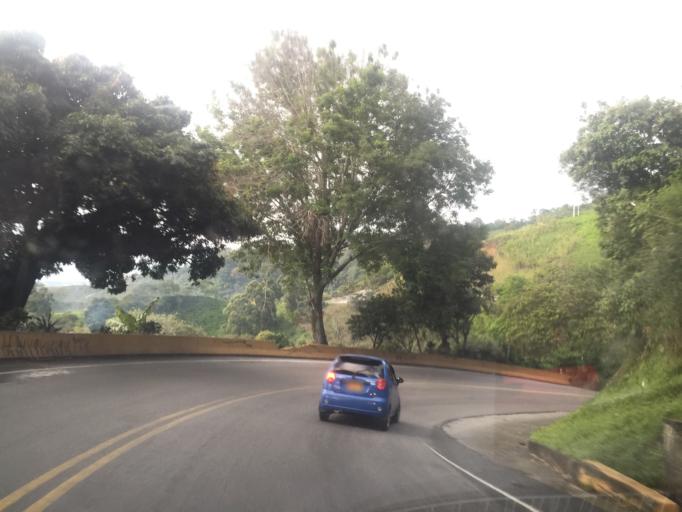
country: CO
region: Quindio
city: Calarca
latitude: 4.5270
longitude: -75.6259
